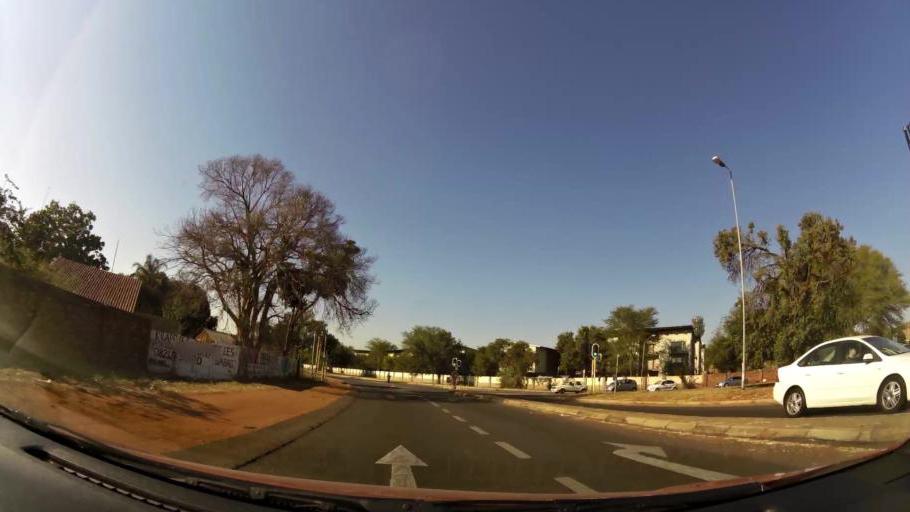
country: ZA
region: Gauteng
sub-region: City of Tshwane Metropolitan Municipality
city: Pretoria
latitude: -25.6687
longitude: 28.1567
